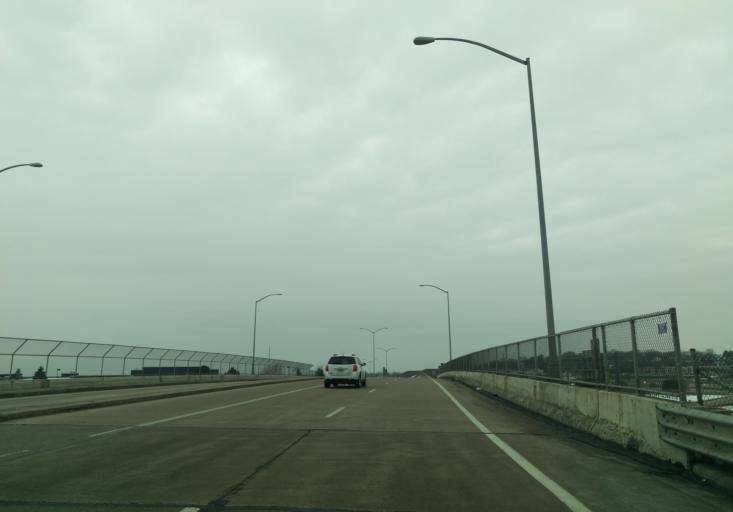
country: US
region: Wisconsin
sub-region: Dane County
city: Monona
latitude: 43.1344
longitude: -89.2934
